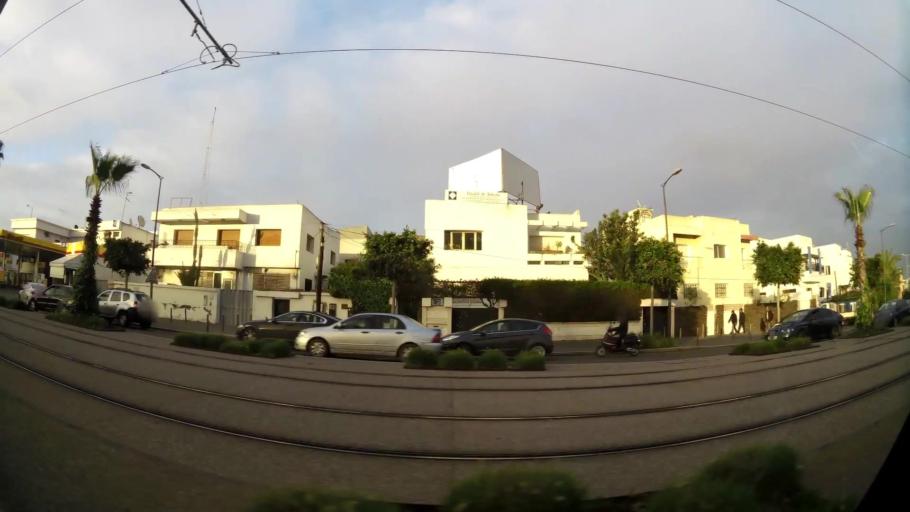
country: MA
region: Grand Casablanca
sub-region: Casablanca
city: Casablanca
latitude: 33.5709
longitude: -7.6688
